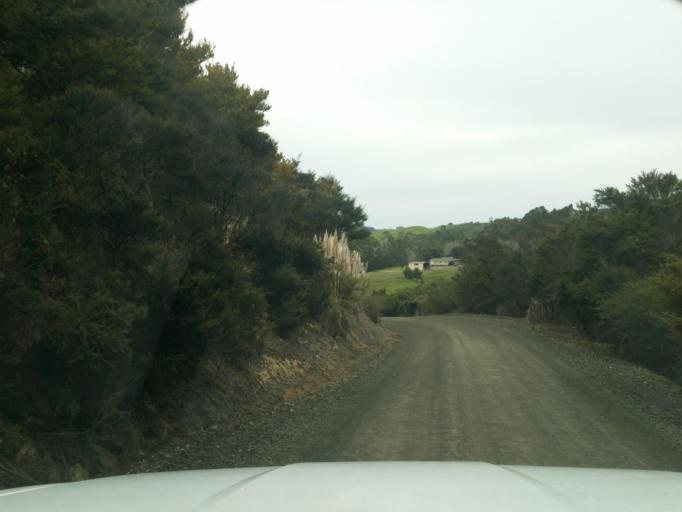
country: NZ
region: Northland
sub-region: Whangarei
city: Maungatapere
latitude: -35.8079
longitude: 174.0421
